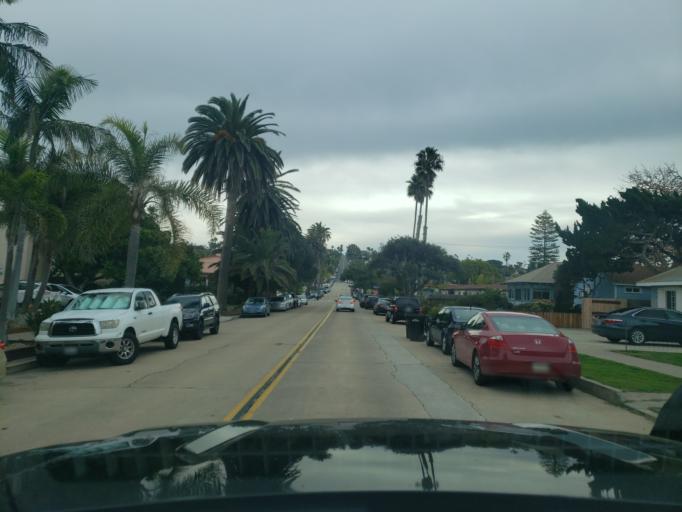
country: US
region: California
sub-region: San Diego County
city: Coronado
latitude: 32.7421
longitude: -117.2538
